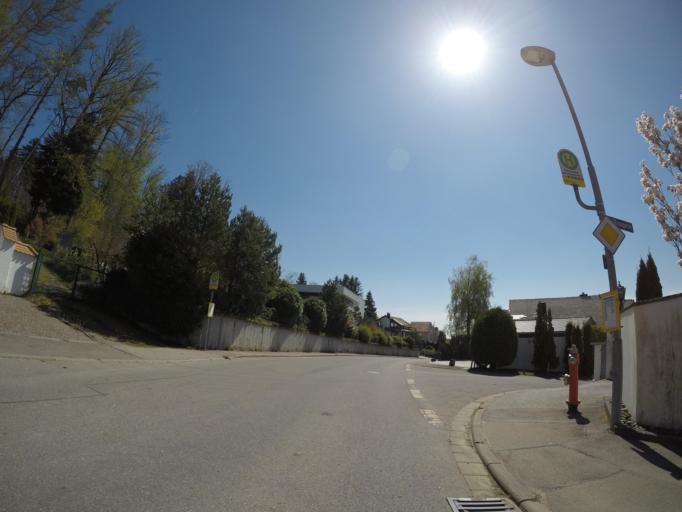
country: DE
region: Baden-Wuerttemberg
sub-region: Tuebingen Region
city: Markdorf
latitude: 47.7344
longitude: 9.3868
